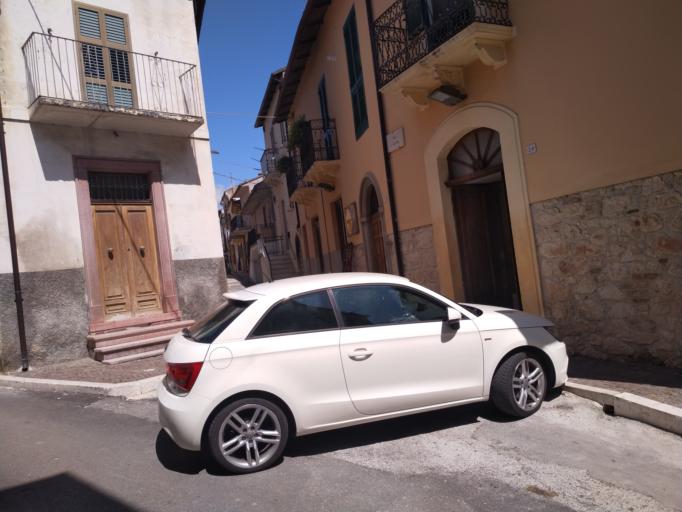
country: IT
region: Abruzzo
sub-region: Provincia dell' Aquila
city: Castelvecchio Subequo
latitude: 42.1309
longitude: 13.7301
